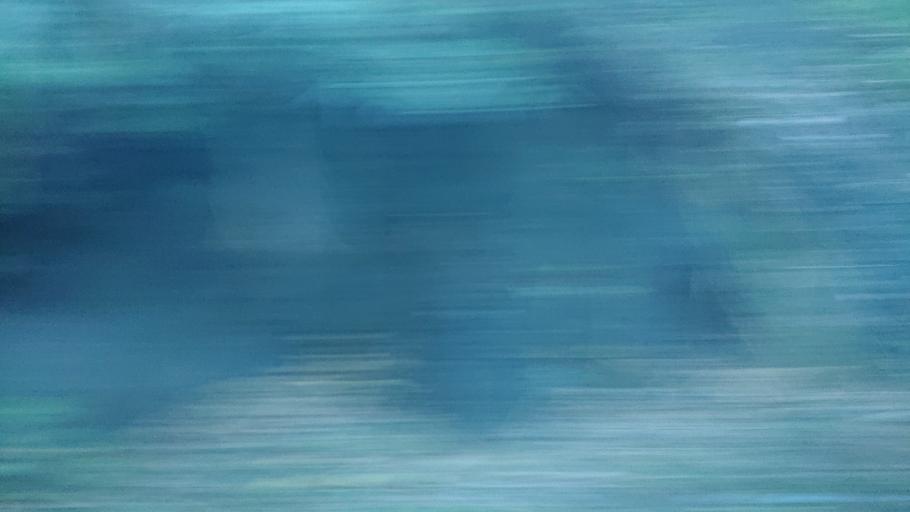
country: TW
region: Taiwan
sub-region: Yunlin
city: Douliu
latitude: 23.5325
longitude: 120.6602
